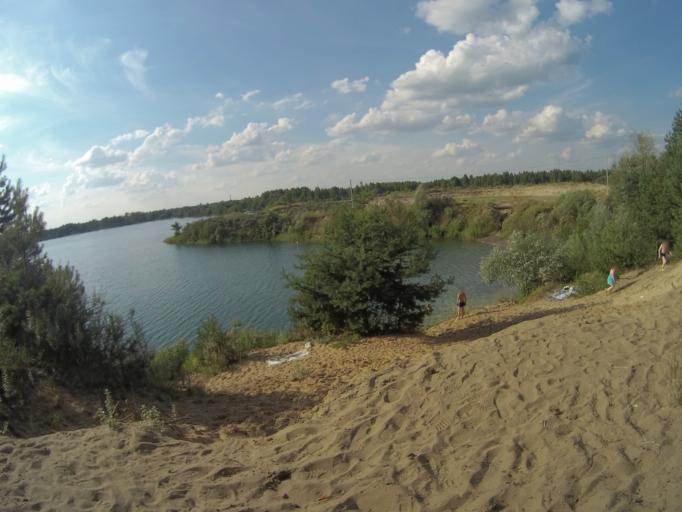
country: RU
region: Vladimir
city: Golovino
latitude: 56.0369
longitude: 40.4202
